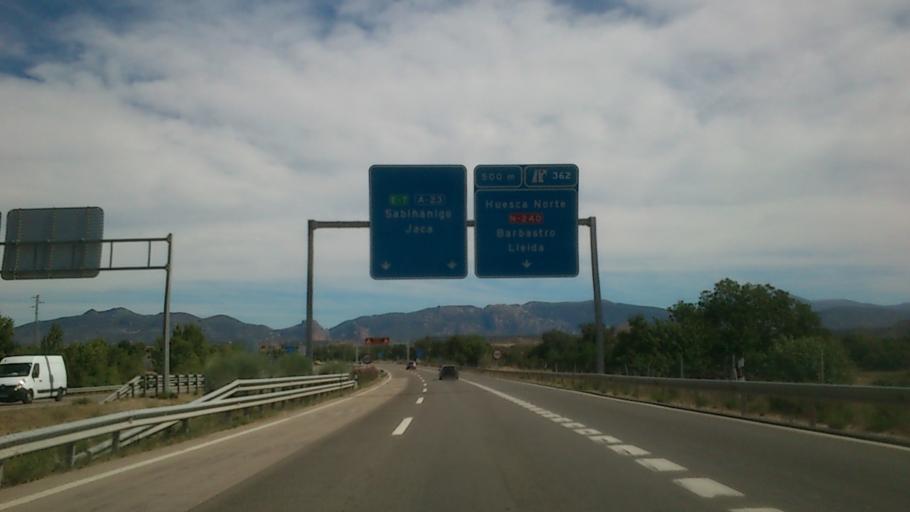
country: ES
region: Aragon
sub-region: Provincia de Huesca
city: Huesca
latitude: 42.1518
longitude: -0.4243
